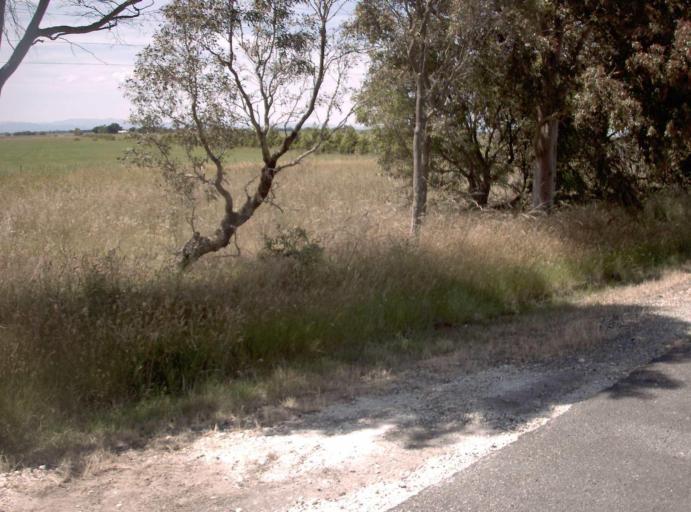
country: AU
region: Victoria
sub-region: Wellington
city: Heyfield
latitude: -38.1150
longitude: 146.8738
